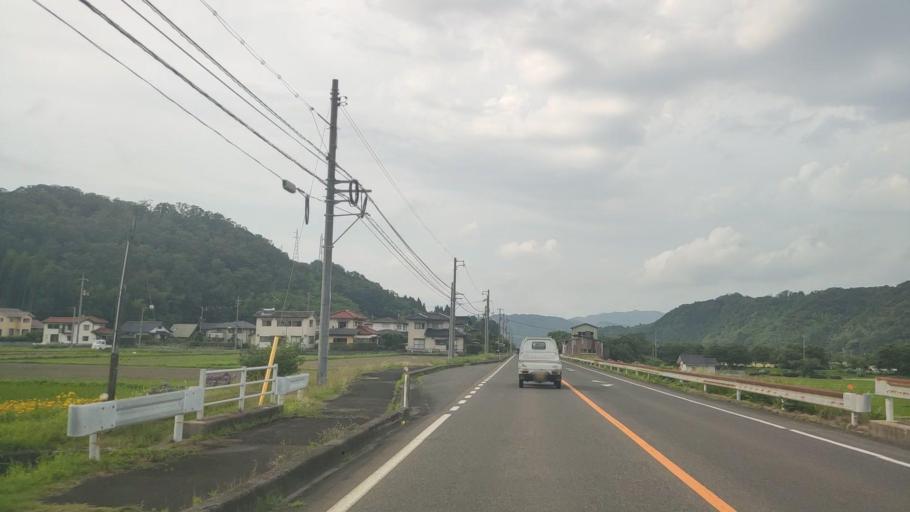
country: JP
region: Tottori
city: Kurayoshi
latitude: 35.3853
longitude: 133.8561
